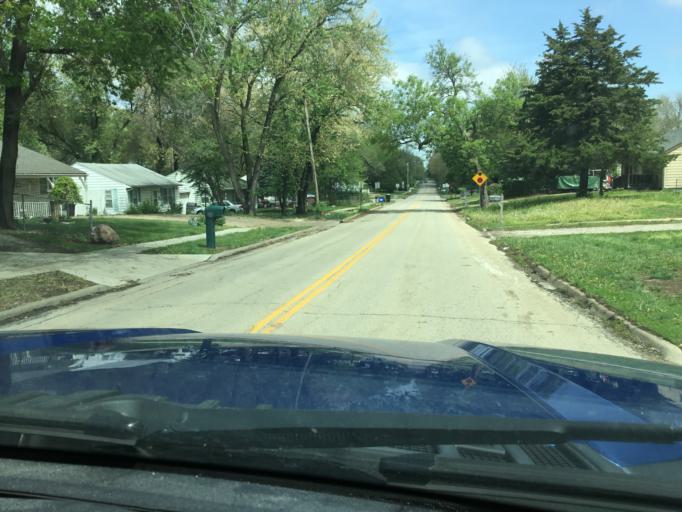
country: US
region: Kansas
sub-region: Shawnee County
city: Topeka
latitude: 39.0215
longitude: -95.6608
